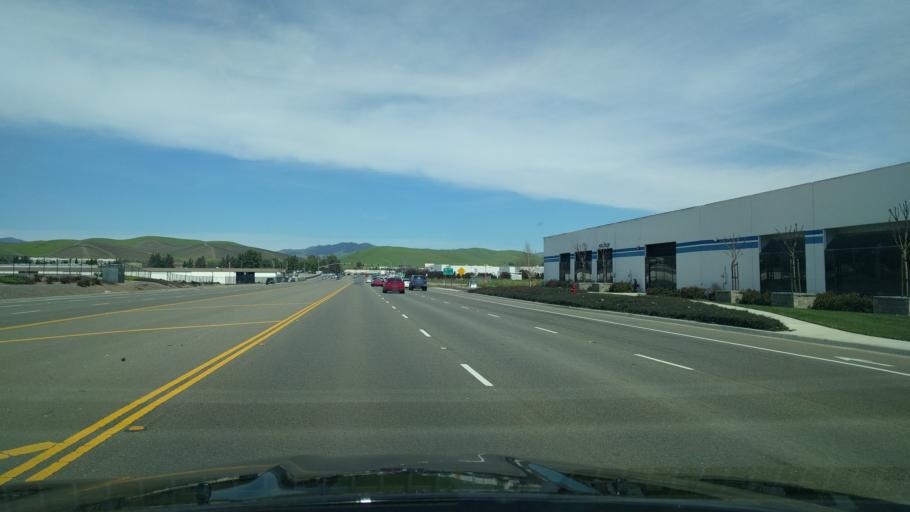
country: US
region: California
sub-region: Alameda County
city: Livermore
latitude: 37.6920
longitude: -121.8054
